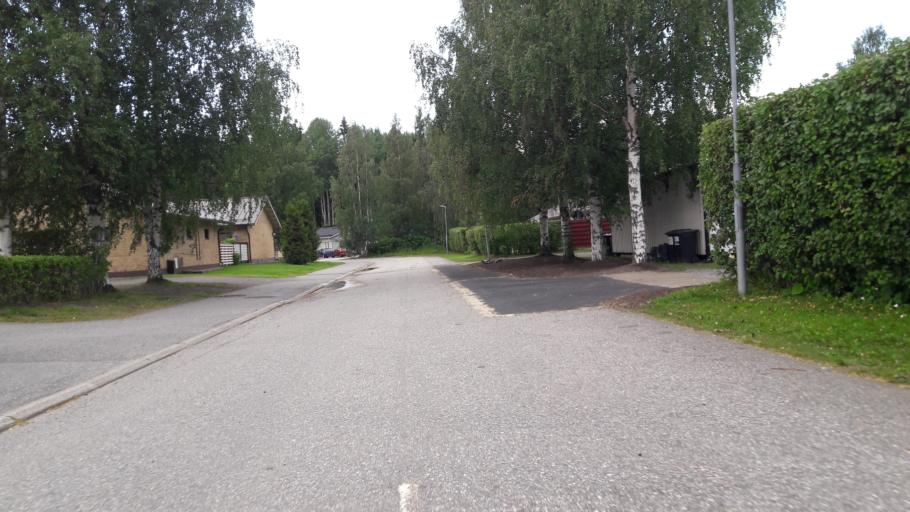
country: FI
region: North Karelia
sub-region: Joensuu
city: Joensuu
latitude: 62.5924
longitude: 29.8010
